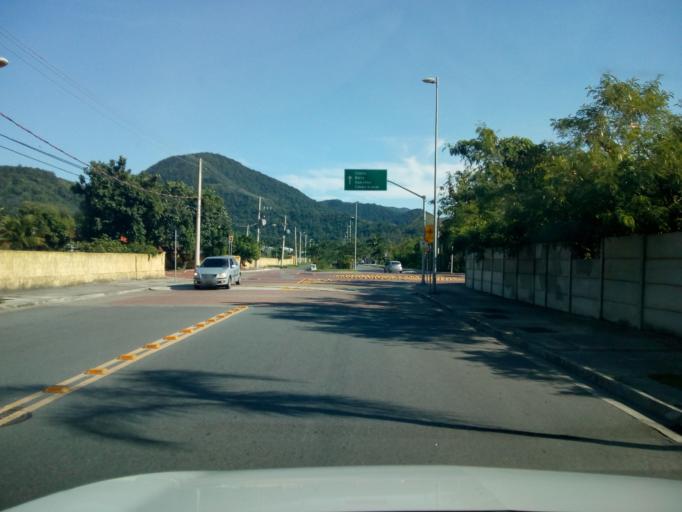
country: BR
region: Rio de Janeiro
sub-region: Nilopolis
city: Nilopolis
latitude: -23.0237
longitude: -43.5141
